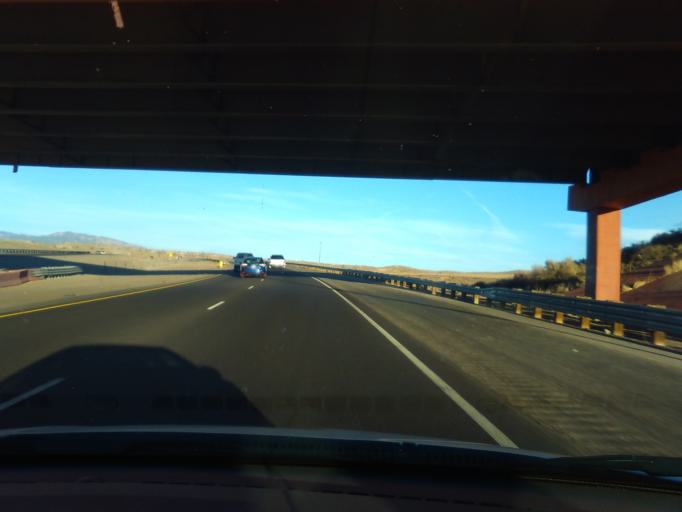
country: US
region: New Mexico
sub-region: Bernalillo County
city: South Valley
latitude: 34.9523
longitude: -106.6646
